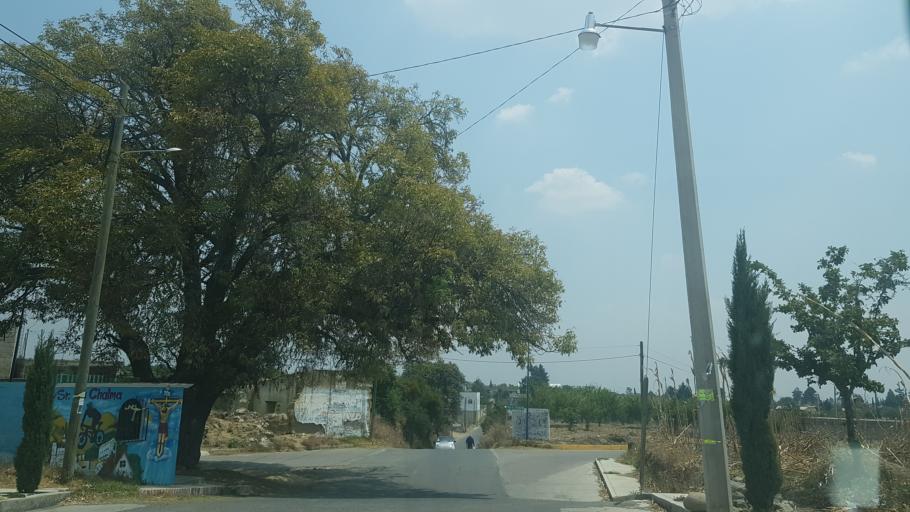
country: MX
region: Puebla
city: San Andres Calpan
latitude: 19.1033
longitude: -98.4713
